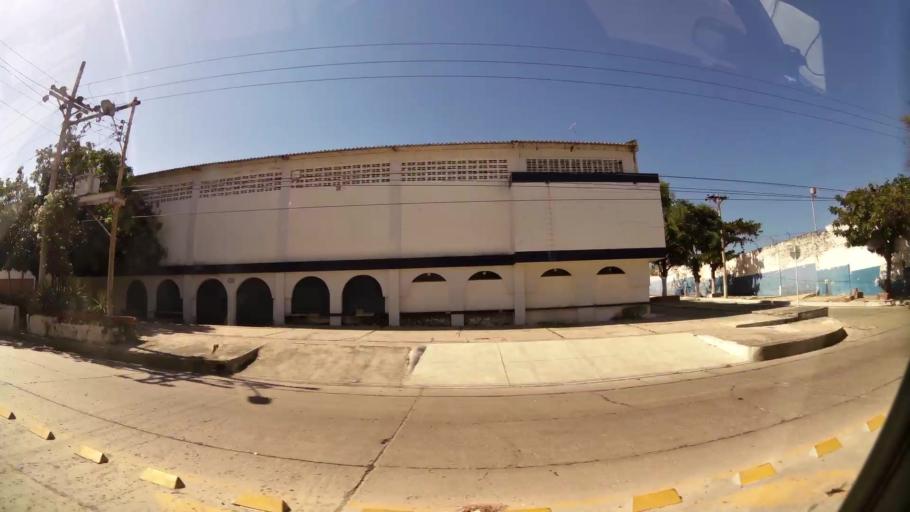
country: CO
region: Atlantico
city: Barranquilla
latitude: 11.0010
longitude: -74.7880
